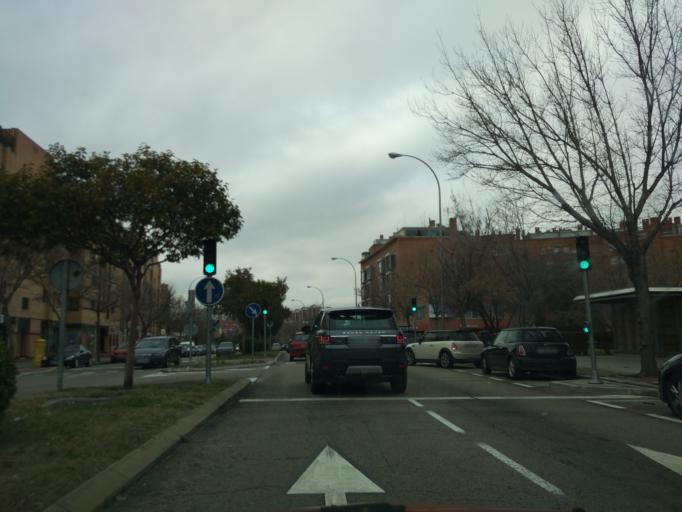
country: ES
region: Madrid
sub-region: Provincia de Madrid
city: San Blas
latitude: 40.4583
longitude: -3.6254
